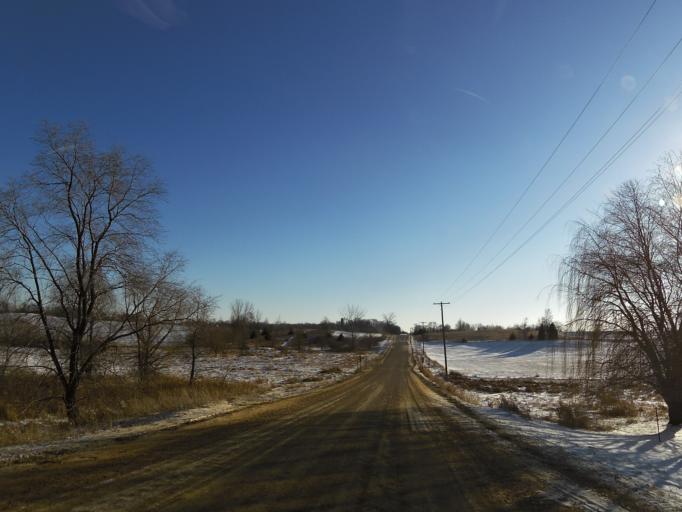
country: US
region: Minnesota
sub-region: Le Sueur County
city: New Prague
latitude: 44.5508
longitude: -93.5529
